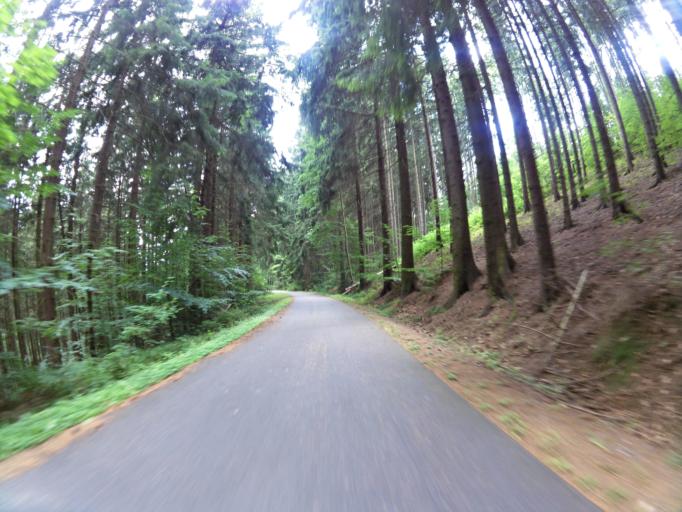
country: DE
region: Thuringia
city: Burgk
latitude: 50.5290
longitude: 11.7567
